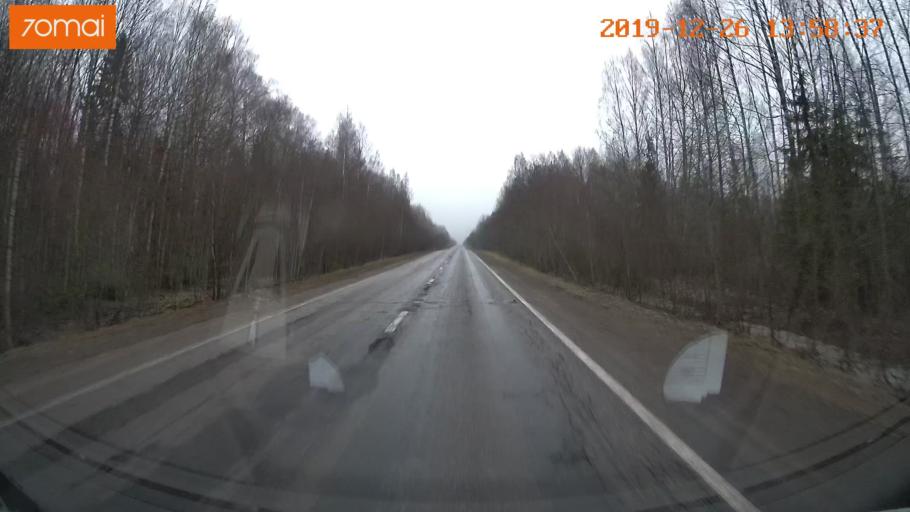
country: RU
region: Jaroslavl
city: Poshekhon'ye
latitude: 58.5726
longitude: 38.7047
